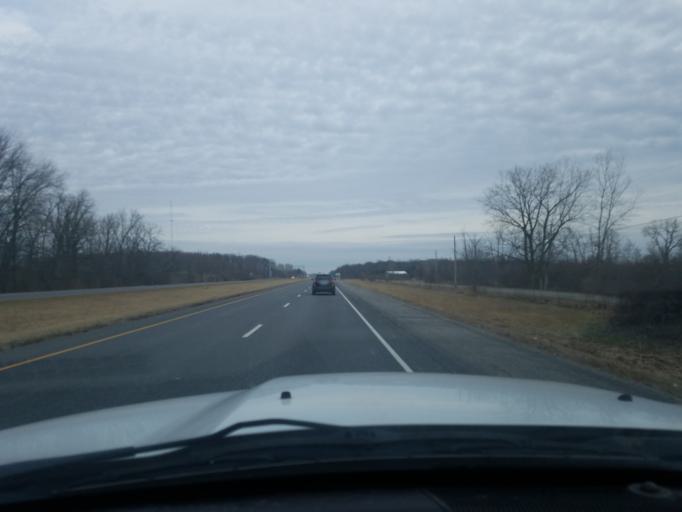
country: US
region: Indiana
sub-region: Huntington County
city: Roanoke
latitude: 40.9755
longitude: -85.2802
